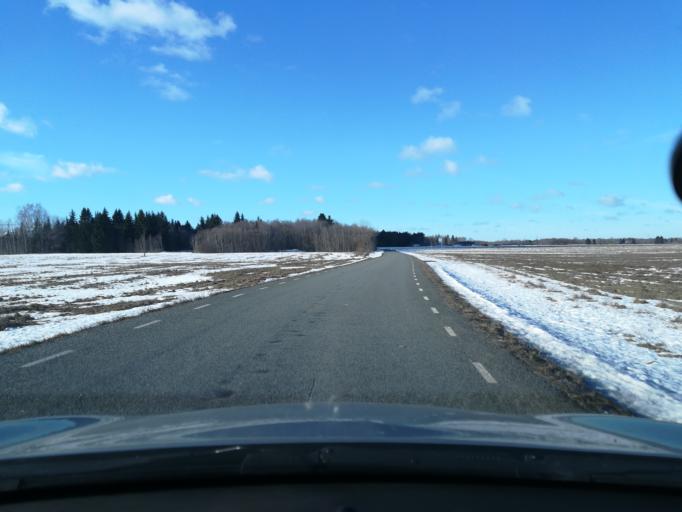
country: EE
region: Harju
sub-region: Kiili vald
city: Kiili
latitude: 59.2628
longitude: 24.8191
